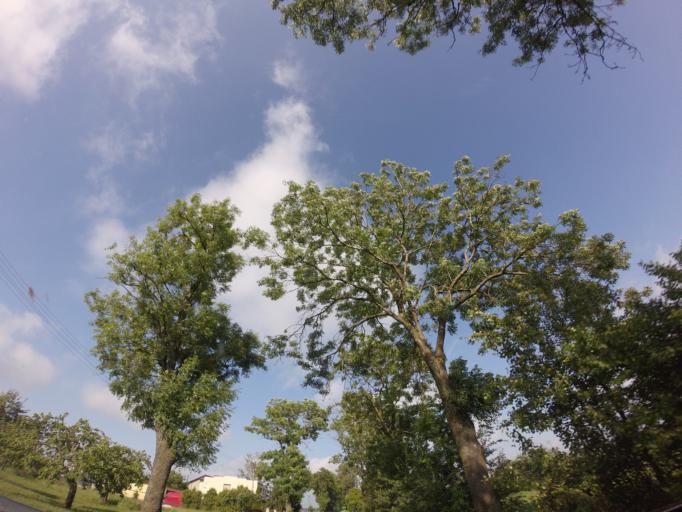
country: PL
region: Lodz Voivodeship
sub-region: Powiat kutnowski
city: Lanieta
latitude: 52.3605
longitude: 19.2599
